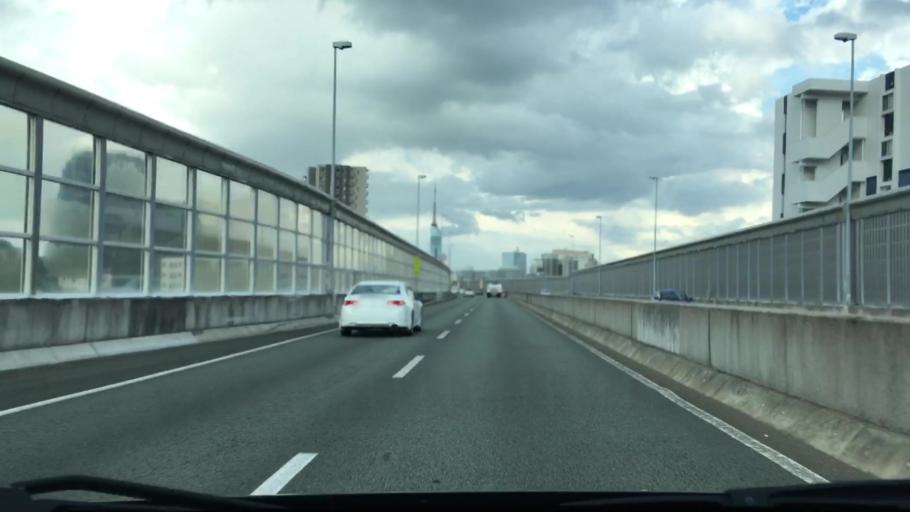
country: JP
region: Fukuoka
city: Fukuoka-shi
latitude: 33.5822
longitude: 130.3374
